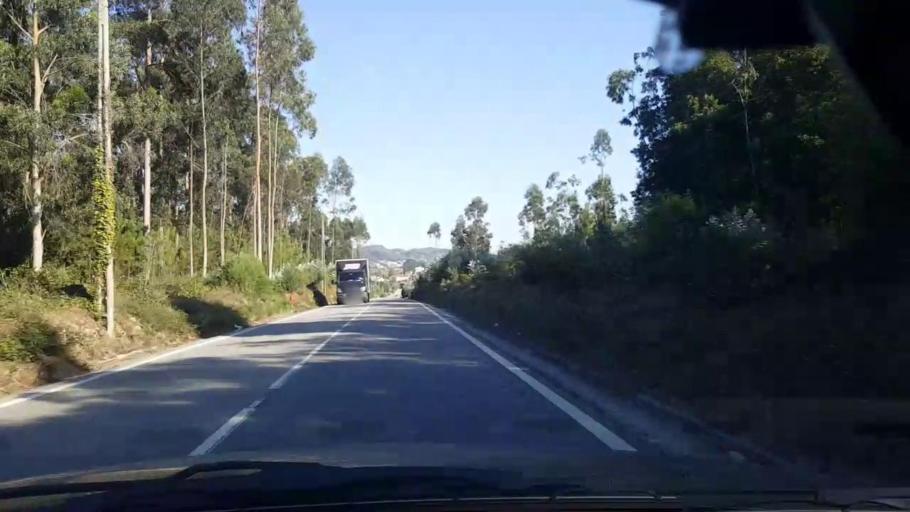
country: PT
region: Porto
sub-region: Vila do Conde
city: Arvore
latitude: 41.3358
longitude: -8.6751
